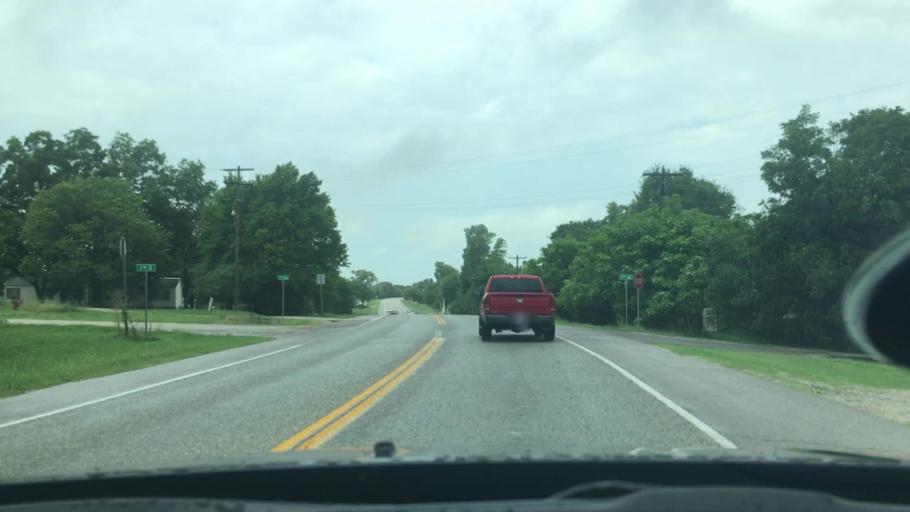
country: US
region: Oklahoma
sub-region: Johnston County
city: Tishomingo
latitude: 34.2444
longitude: -96.7526
